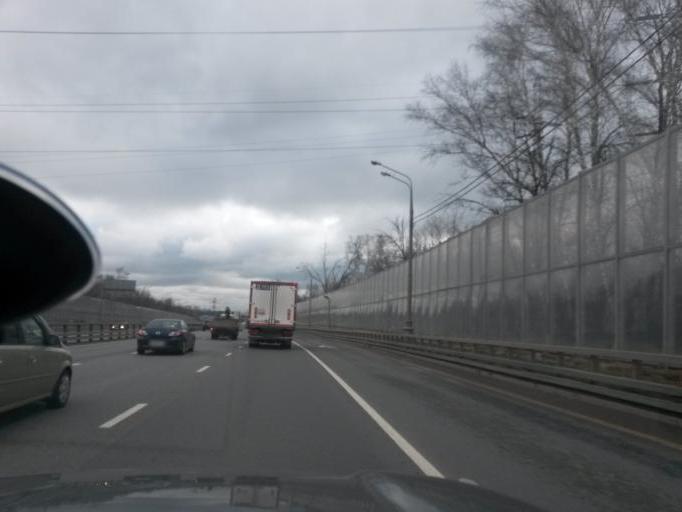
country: RU
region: Moscow
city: Annino
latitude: 55.5608
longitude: 37.5926
